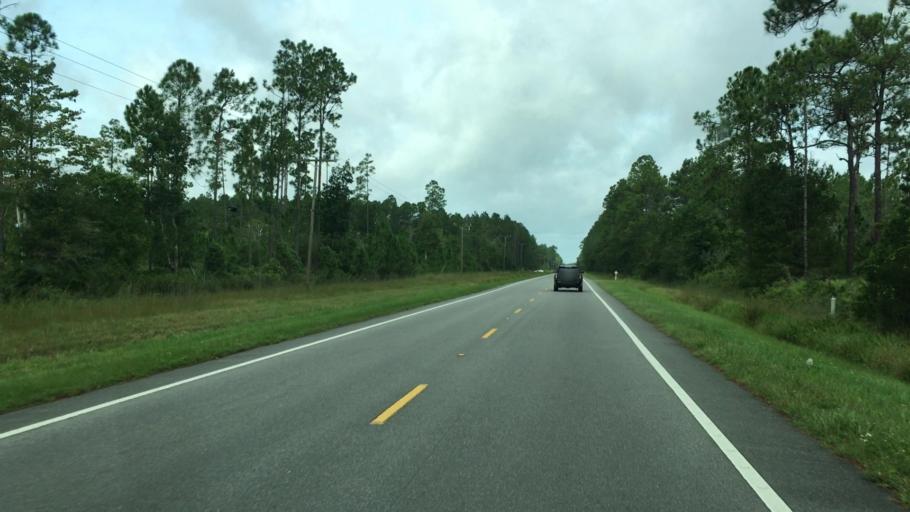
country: US
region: Florida
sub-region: Flagler County
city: Bunnell
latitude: 29.4714
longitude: -81.3216
